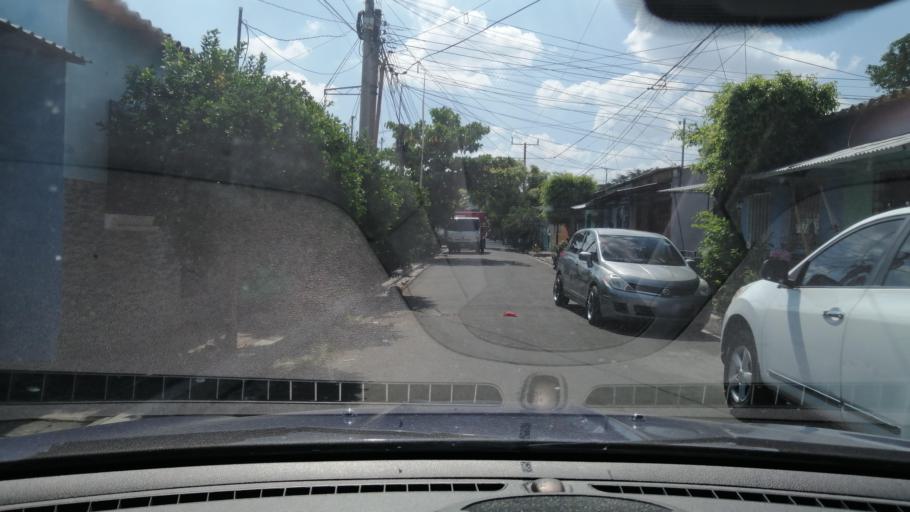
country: SV
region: Santa Ana
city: Metapan
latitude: 14.3347
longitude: -89.4520
